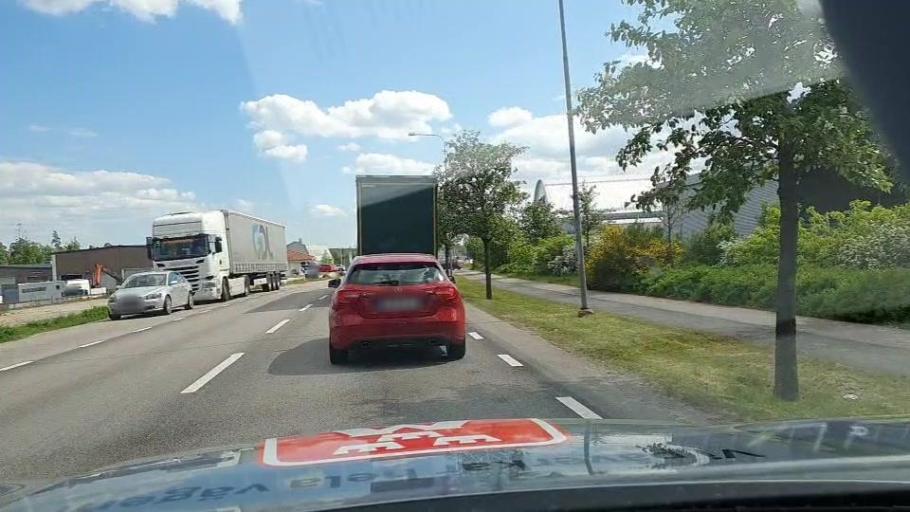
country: SE
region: Kronoberg
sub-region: Ljungby Kommun
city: Ljungby
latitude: 56.8150
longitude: 13.9084
